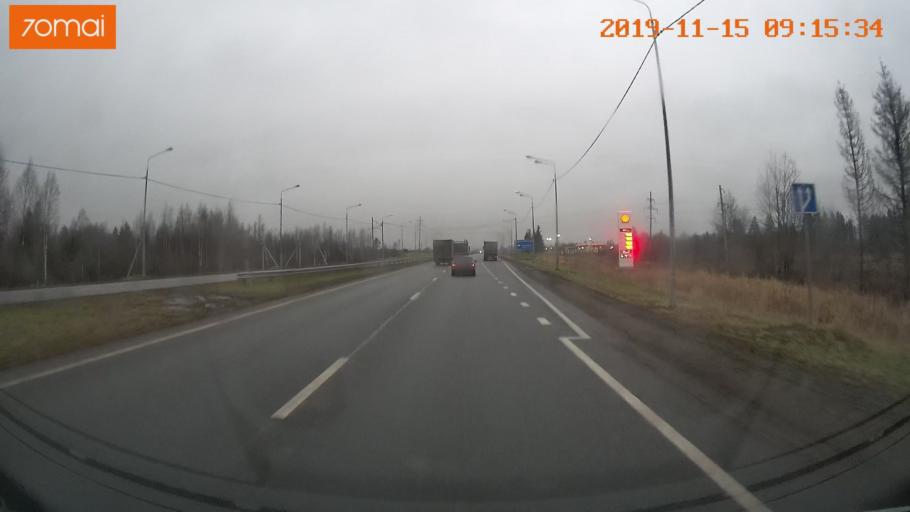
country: RU
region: Vologda
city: Tonshalovo
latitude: 59.2404
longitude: 37.9676
